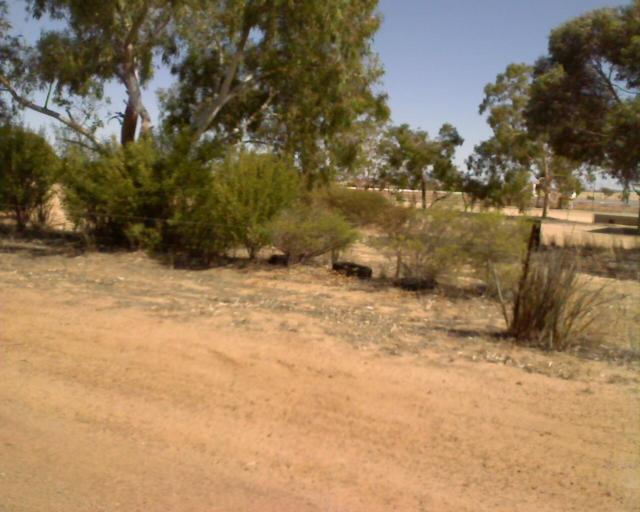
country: AU
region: Western Australia
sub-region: Wongan-Ballidu
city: Wongan Hills
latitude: -30.3850
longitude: 116.6732
